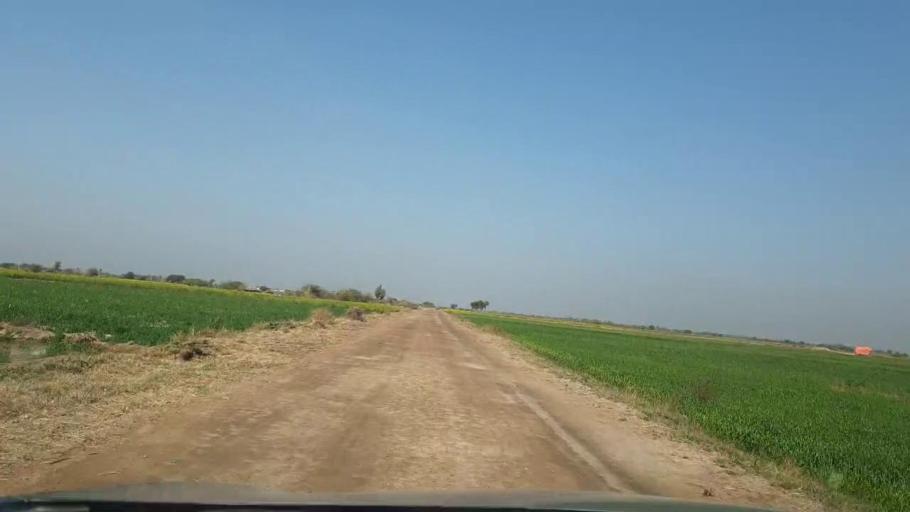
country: PK
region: Sindh
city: Berani
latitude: 25.7070
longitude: 68.8640
